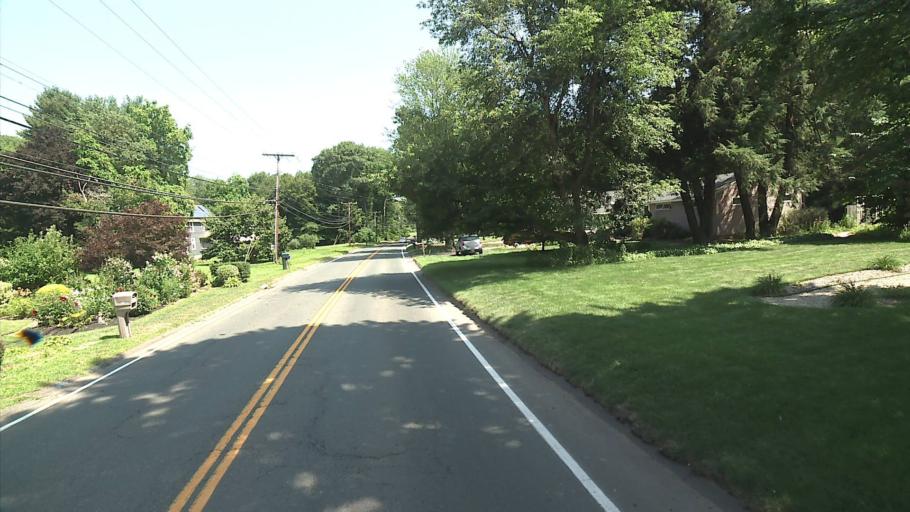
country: US
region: Connecticut
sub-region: Hartford County
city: Windsor
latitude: 41.8586
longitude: -72.6849
